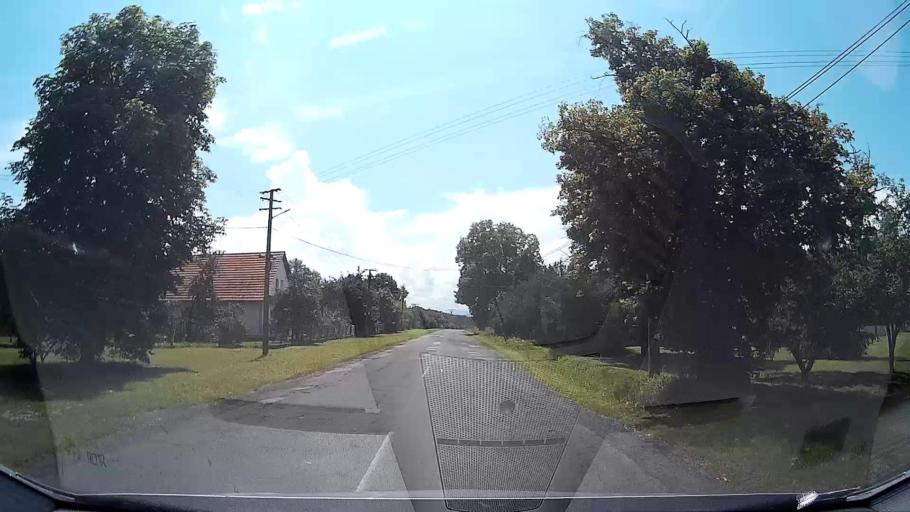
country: SK
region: Banskobystricky
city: Fil'akovo
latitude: 48.3263
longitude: 19.8167
